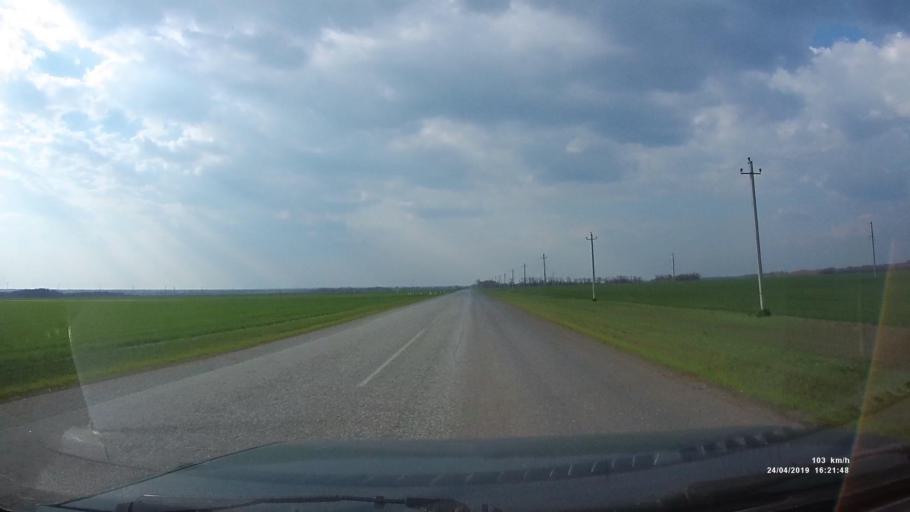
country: RU
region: Rostov
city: Orlovskiy
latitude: 46.8102
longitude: 42.0620
